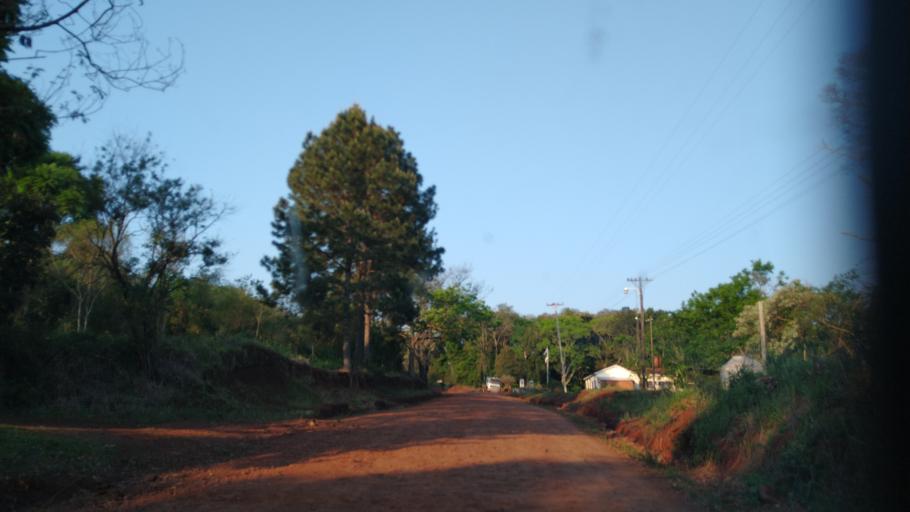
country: AR
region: Misiones
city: Jardin America
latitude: -27.0892
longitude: -55.2794
